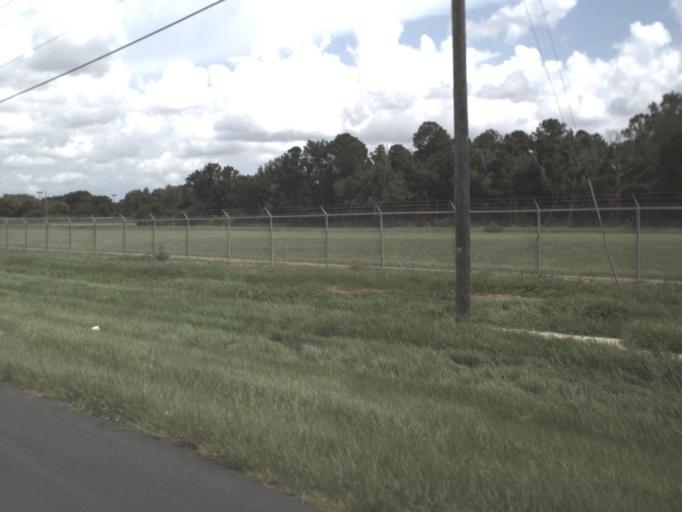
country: US
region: Florida
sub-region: Hillsborough County
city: Egypt Lake-Leto
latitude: 27.9962
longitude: -82.5363
